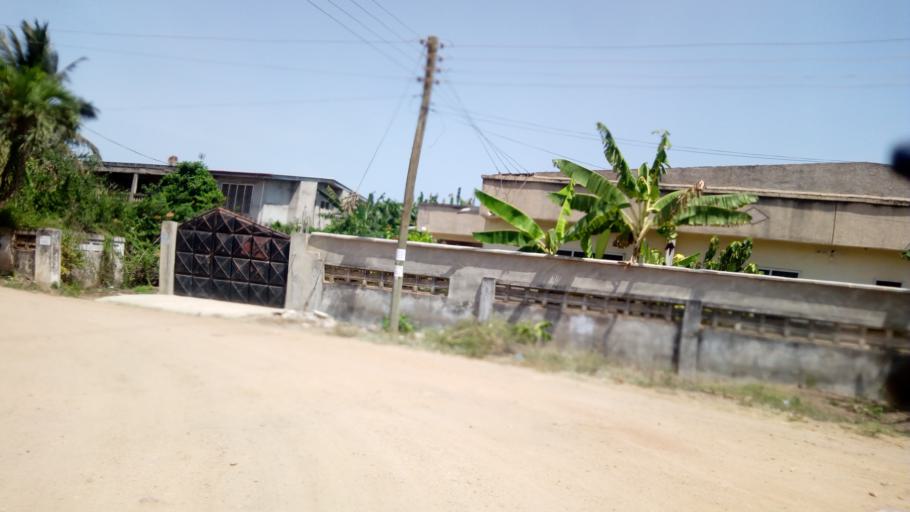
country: GH
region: Central
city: Cape Coast
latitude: 5.1307
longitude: -1.2814
